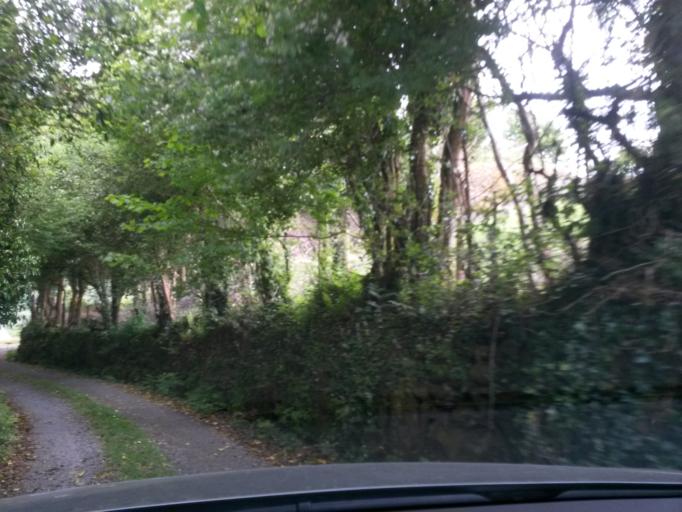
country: IE
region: Munster
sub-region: Ciarrai
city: Kenmare
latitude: 51.8177
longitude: -9.5165
